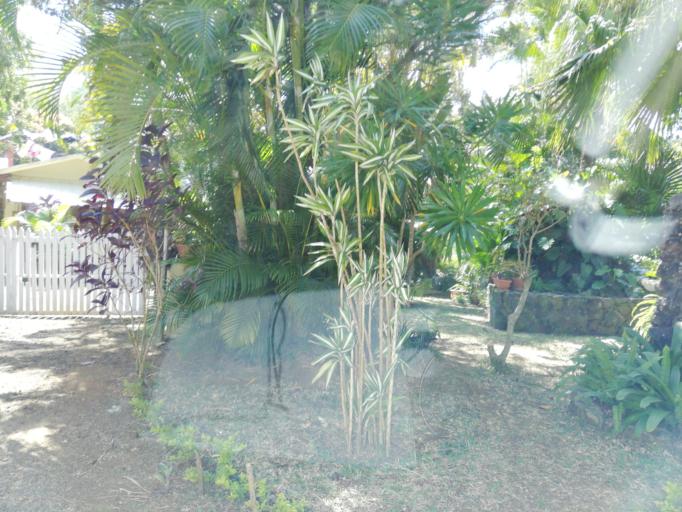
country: MU
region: Moka
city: Moka
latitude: -20.2231
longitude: 57.5080
